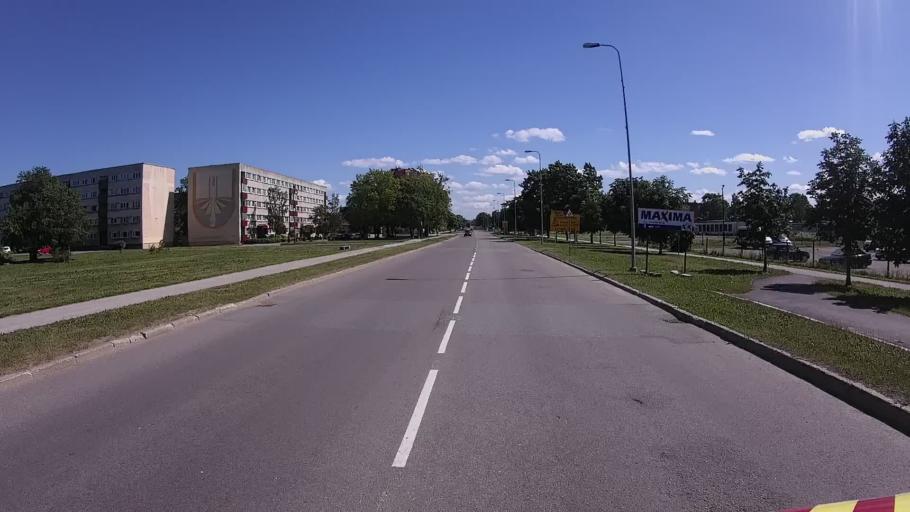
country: EE
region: Ida-Virumaa
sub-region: Kohtla-Jaerve linn
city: Kohtla-Jarve
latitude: 59.4098
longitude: 27.2790
